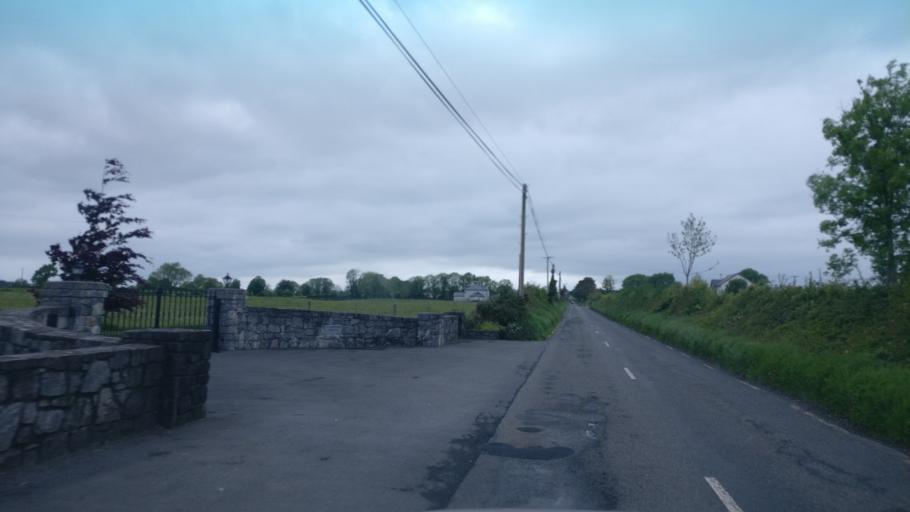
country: IE
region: Connaught
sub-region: County Galway
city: Portumna
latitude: 53.0931
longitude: -8.2368
